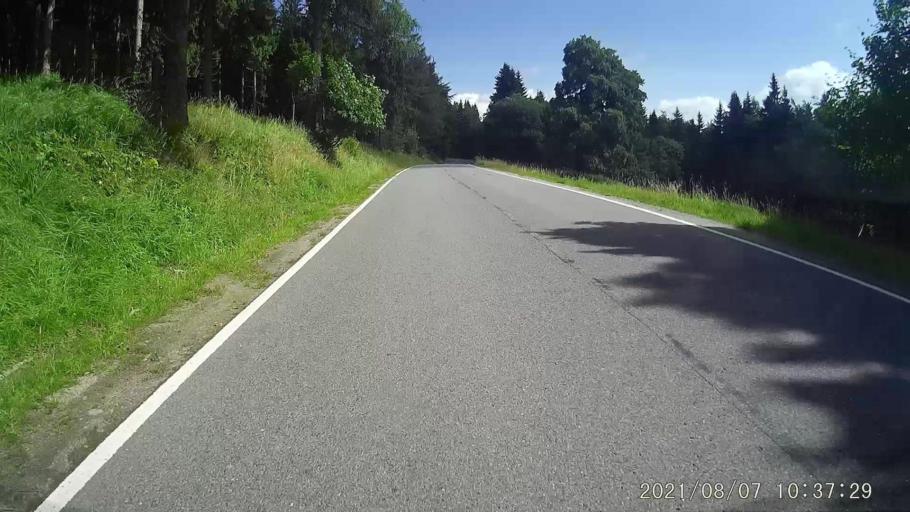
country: PL
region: Lower Silesian Voivodeship
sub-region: Powiat klodzki
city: Duszniki-Zdroj
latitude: 50.3555
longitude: 16.3732
